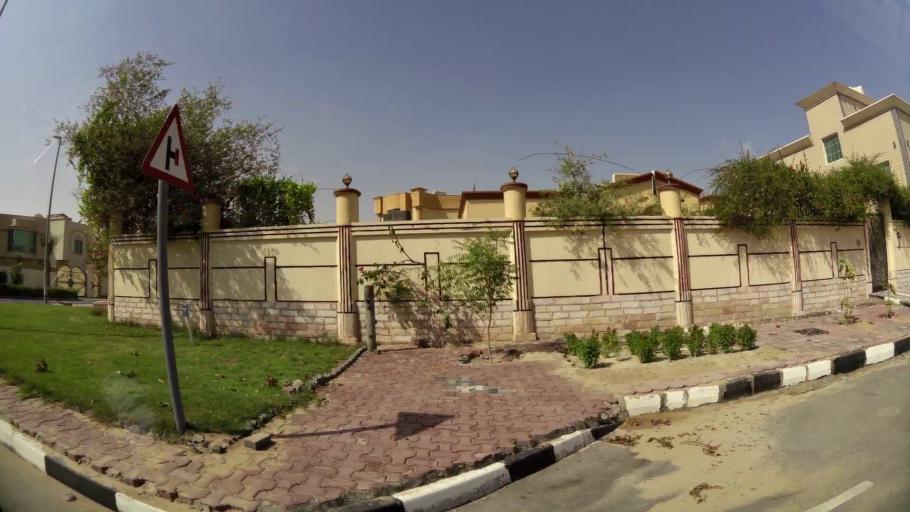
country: AE
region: Ash Shariqah
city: Sharjah
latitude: 25.2042
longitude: 55.4033
